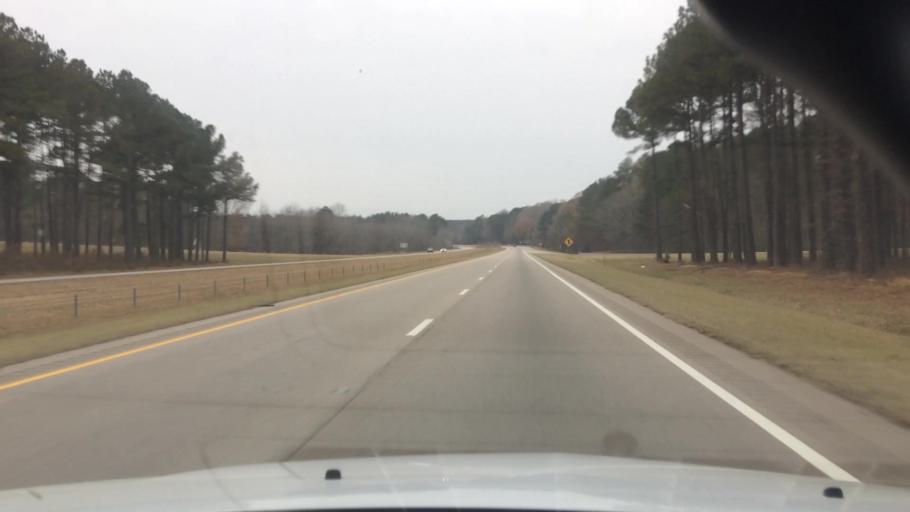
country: US
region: North Carolina
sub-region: Wake County
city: Zebulon
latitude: 35.8611
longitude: -78.2691
